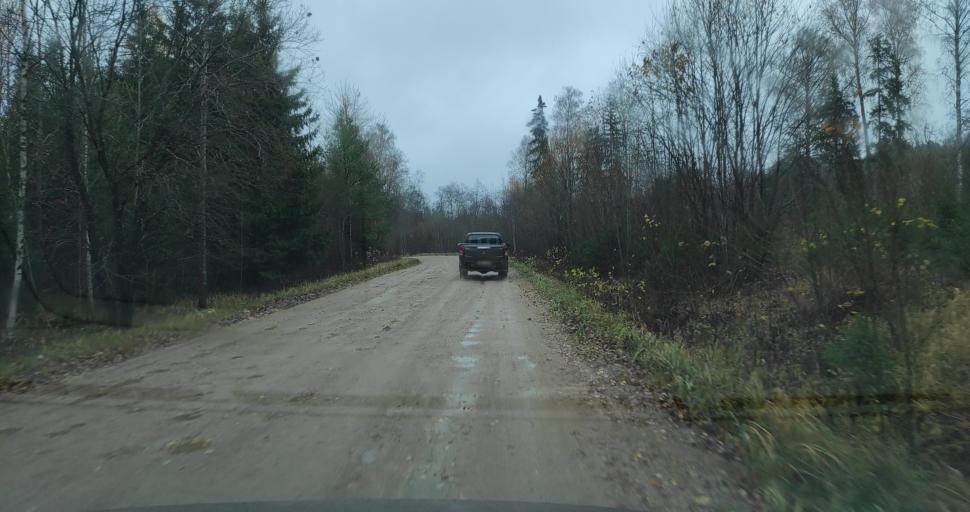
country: LV
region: Skrunda
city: Skrunda
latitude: 56.6857
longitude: 22.0751
